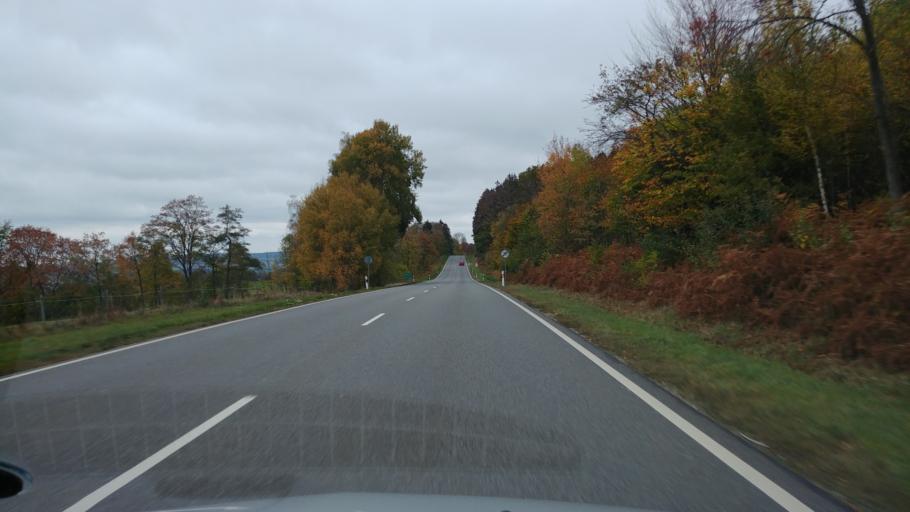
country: DE
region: Rheinland-Pfalz
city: Malborn
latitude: 49.6935
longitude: 6.9763
